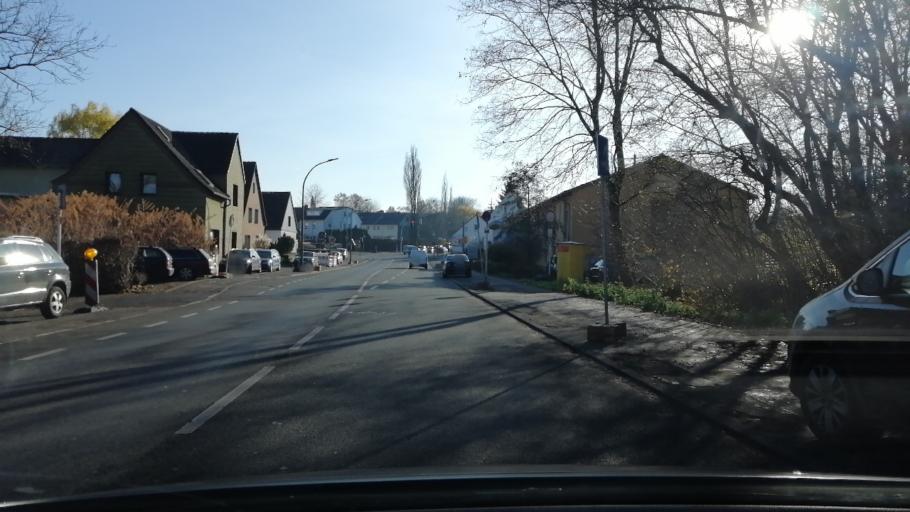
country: DE
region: North Rhine-Westphalia
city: Schwerte
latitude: 51.5082
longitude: 7.5565
